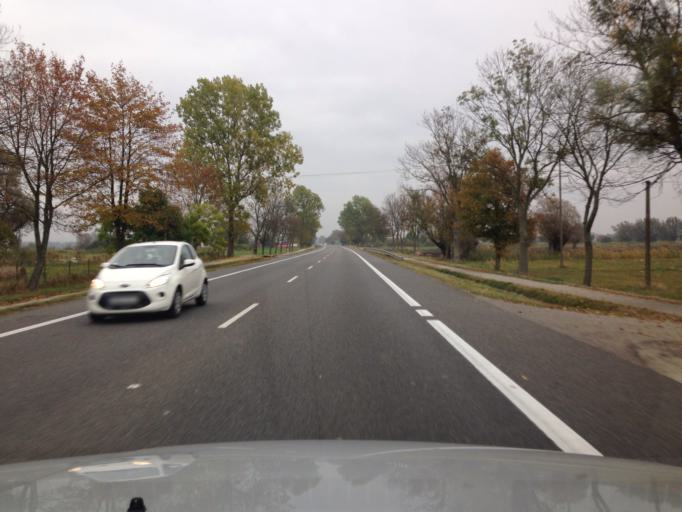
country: PL
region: Warmian-Masurian Voivodeship
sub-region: Powiat elblaski
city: Gronowo Elblaskie
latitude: 54.1671
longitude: 19.3055
